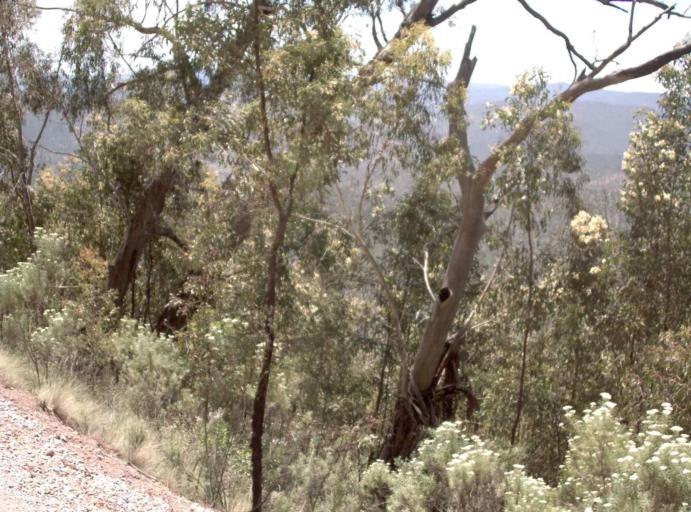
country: AU
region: New South Wales
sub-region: Snowy River
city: Jindabyne
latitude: -37.0071
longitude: 148.2978
